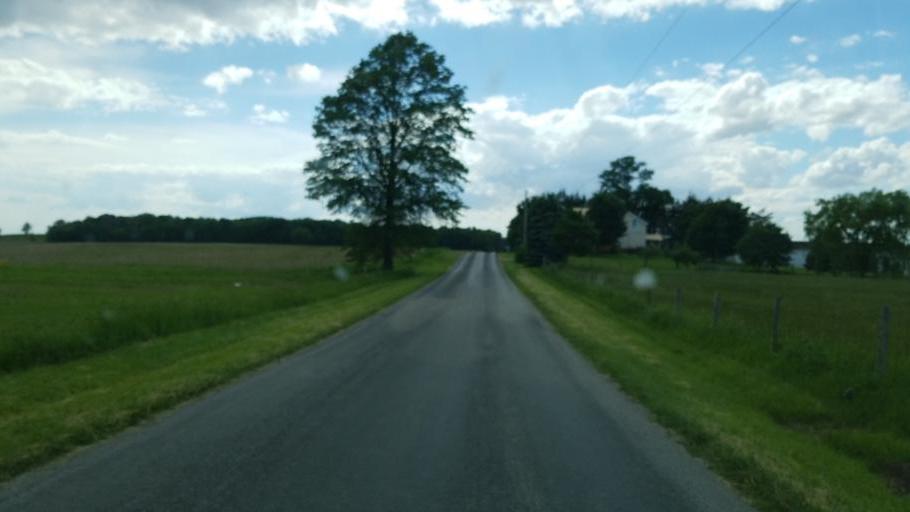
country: US
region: Ohio
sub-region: Huron County
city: Plymouth
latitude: 40.9523
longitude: -82.6404
